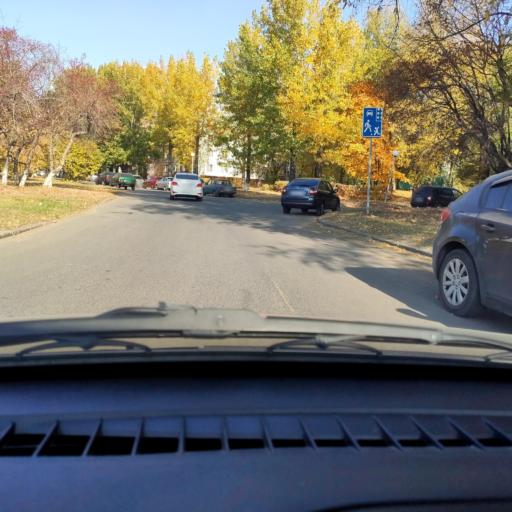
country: RU
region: Samara
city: Tol'yatti
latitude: 53.5104
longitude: 49.2569
